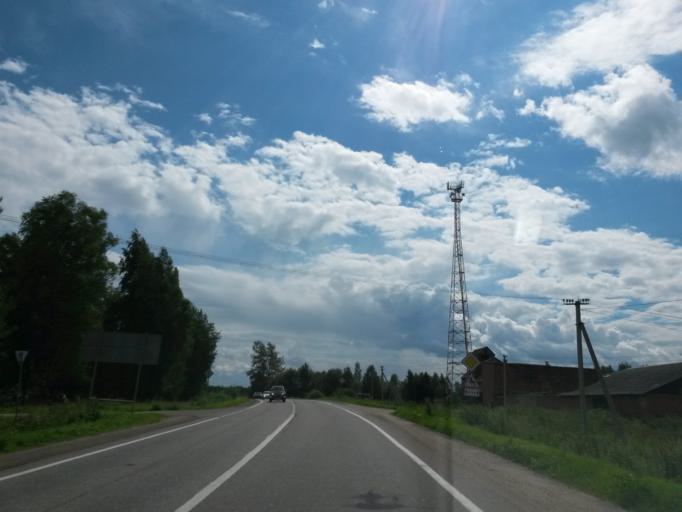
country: RU
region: Jaroslavl
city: Gavrilov-Yam
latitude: 57.3083
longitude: 39.9374
